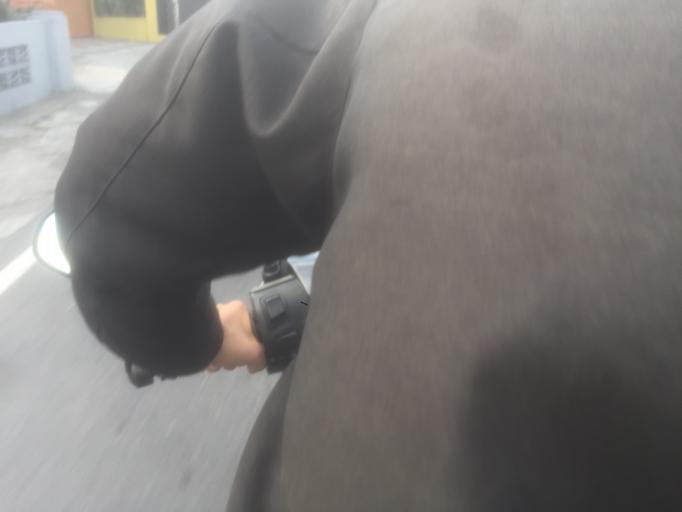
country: ID
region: Daerah Istimewa Yogyakarta
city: Sleman
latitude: -7.6385
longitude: 110.4257
